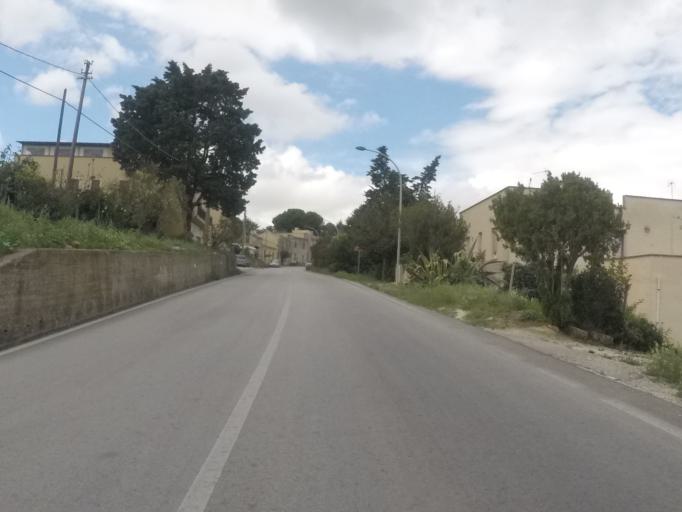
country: IT
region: Sicily
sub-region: Trapani
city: Valderice
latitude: 38.0381
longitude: 12.6578
